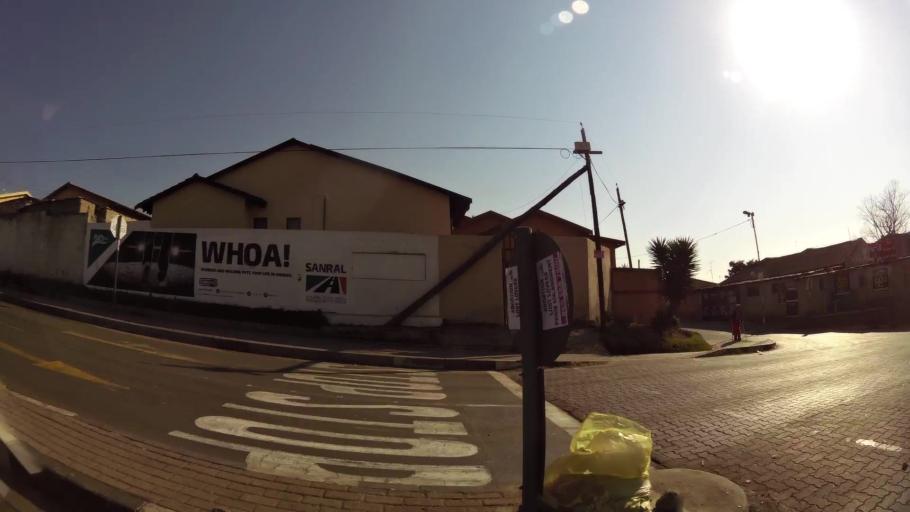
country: ZA
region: Gauteng
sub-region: City of Johannesburg Metropolitan Municipality
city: Modderfontein
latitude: -26.1088
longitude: 28.0978
